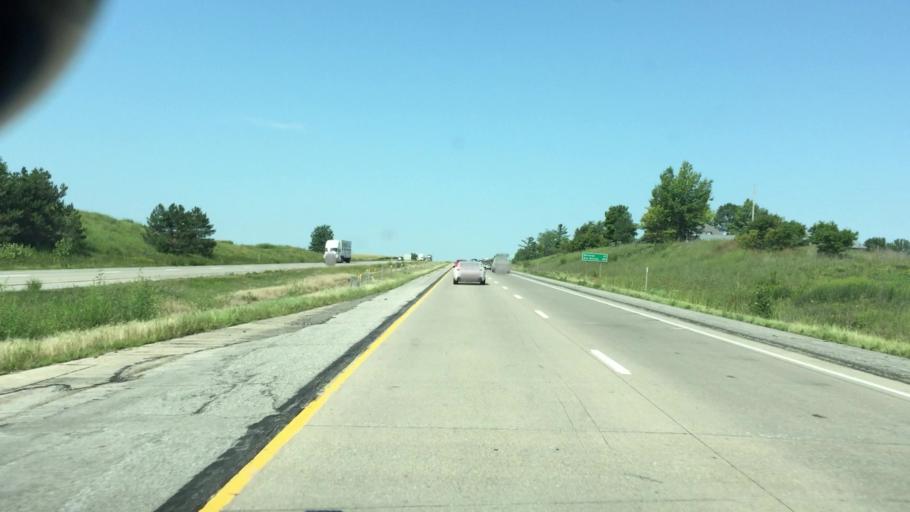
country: US
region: Iowa
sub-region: Iowa County
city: Williamsburg
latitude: 41.6873
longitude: -92.0234
